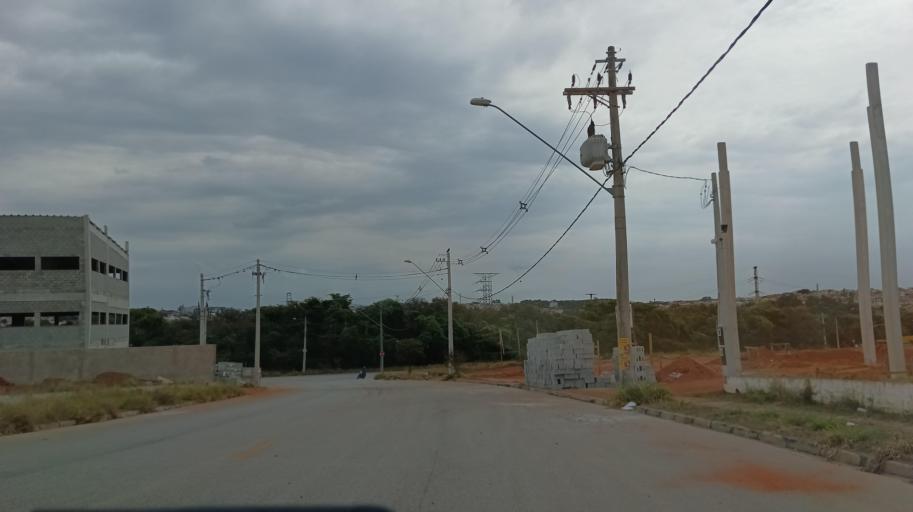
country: BR
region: Sao Paulo
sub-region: Sorocaba
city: Sorocaba
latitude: -23.4538
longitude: -47.4569
